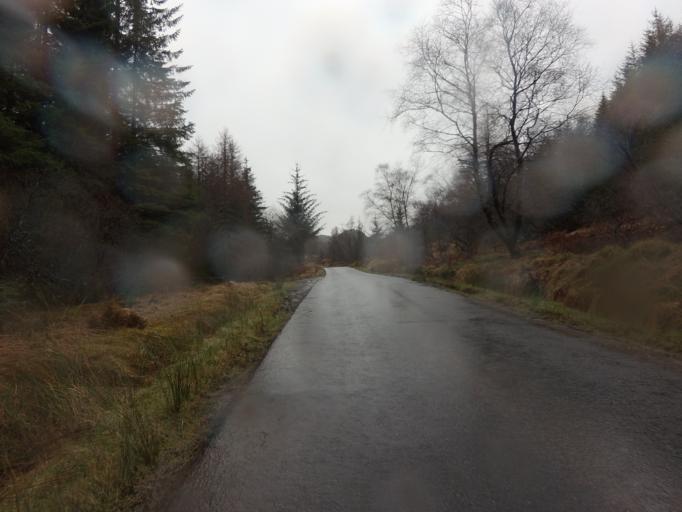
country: GB
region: Scotland
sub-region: West Dunbartonshire
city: Balloch
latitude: 56.2326
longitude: -4.5591
